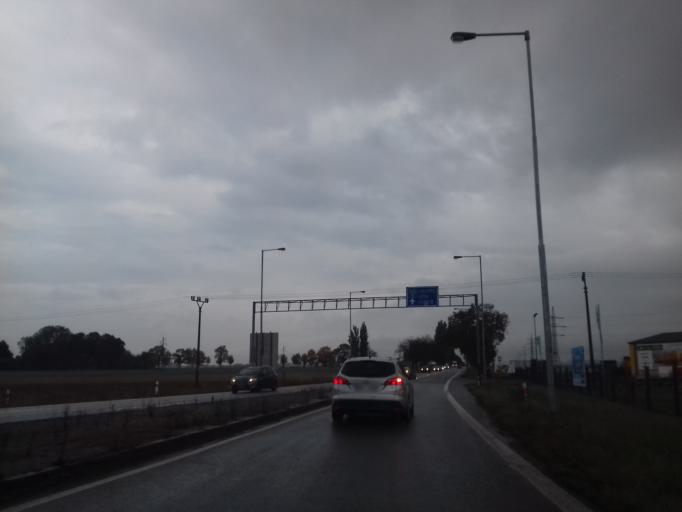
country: CZ
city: Predmerice nad Labem
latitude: 50.2326
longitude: 15.7914
